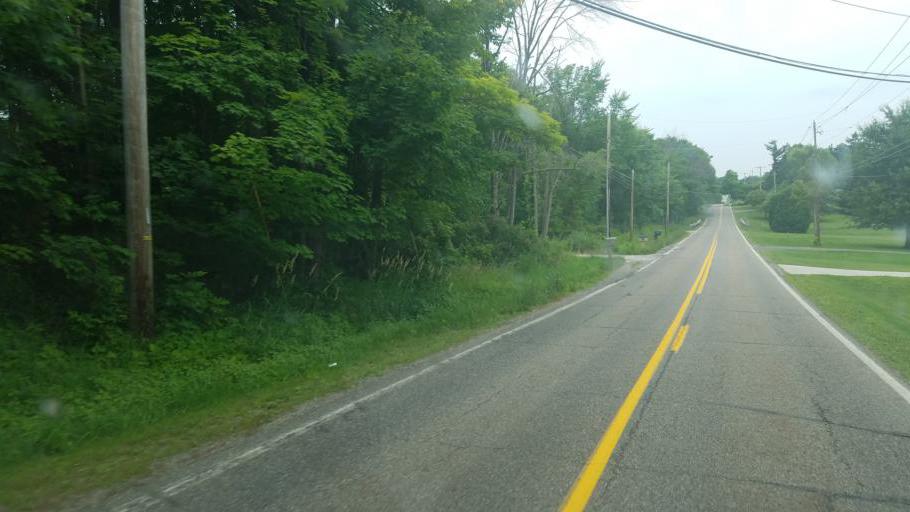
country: US
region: Ohio
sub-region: Portage County
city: Ravenna
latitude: 41.0987
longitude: -81.1811
